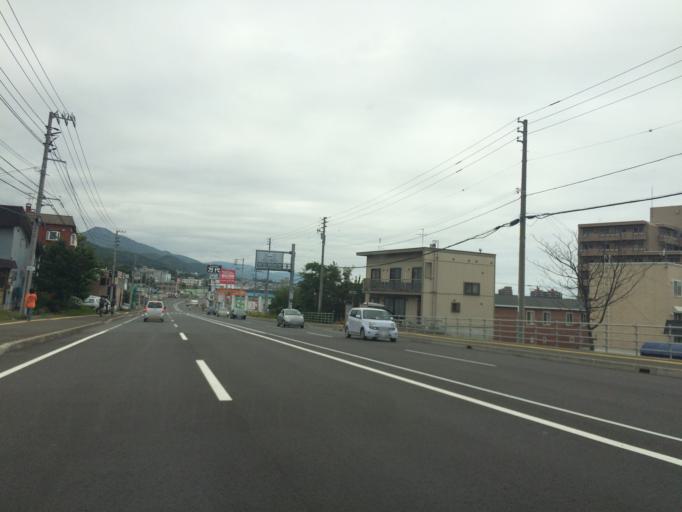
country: JP
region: Hokkaido
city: Sapporo
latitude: 43.1215
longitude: 141.2332
